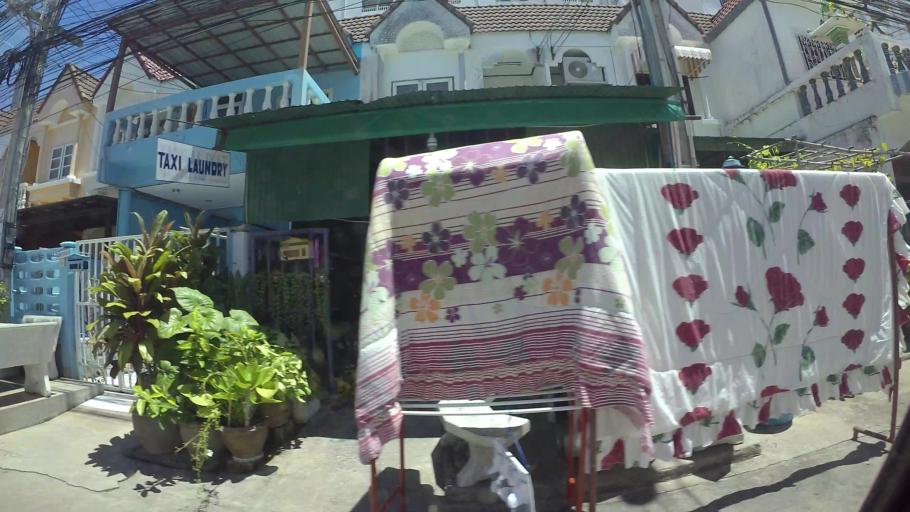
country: TH
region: Chon Buri
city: Phatthaya
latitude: 12.9309
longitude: 100.8931
